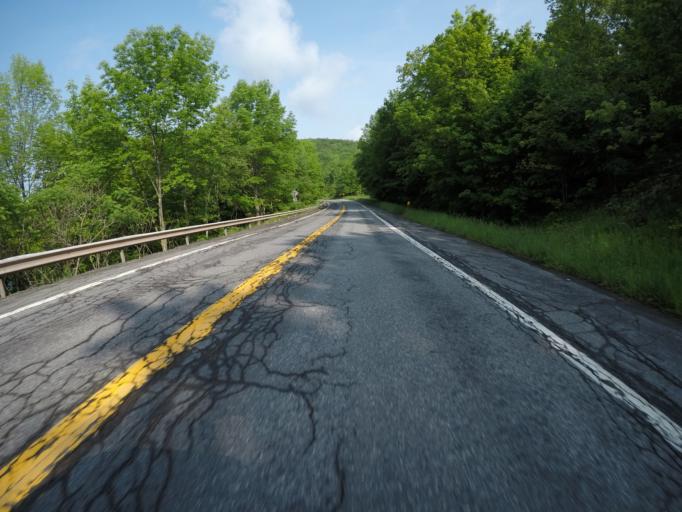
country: US
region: New York
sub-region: Sullivan County
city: Livingston Manor
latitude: 42.1184
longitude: -74.7463
